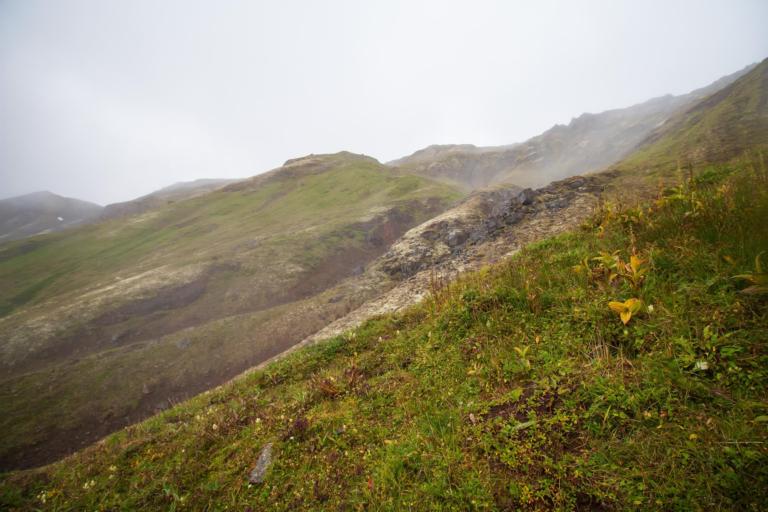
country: RU
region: Kamtsjatka
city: Yelizovo
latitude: 54.0140
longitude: 158.0783
